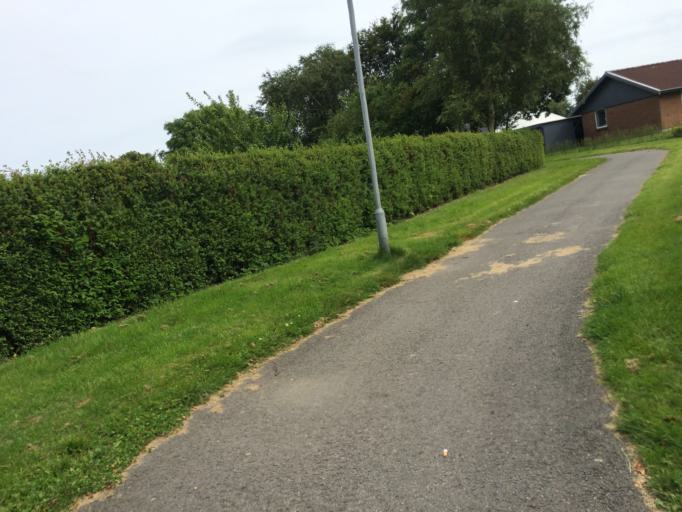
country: DK
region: Central Jutland
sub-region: Holstebro Kommune
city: Ulfborg
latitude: 56.2745
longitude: 8.3112
